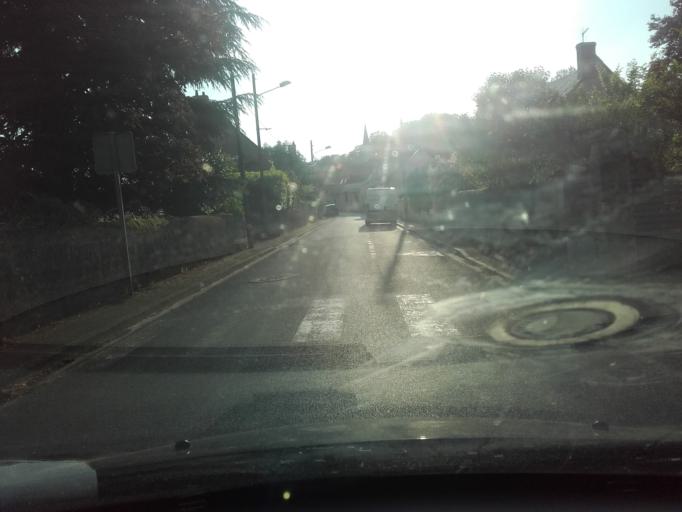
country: FR
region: Centre
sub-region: Departement d'Indre-et-Loire
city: Noizay
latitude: 47.4216
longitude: 0.8944
